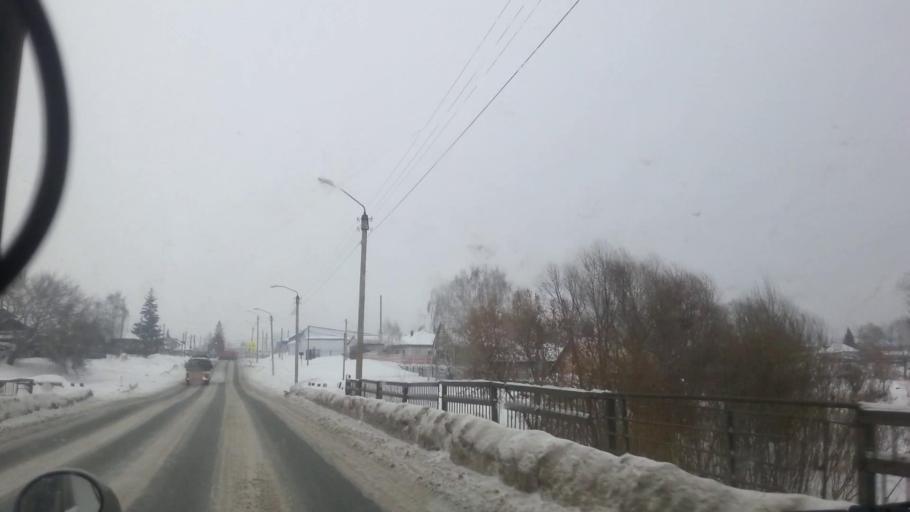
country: RU
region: Altai Krai
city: Vlasikha
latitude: 53.2953
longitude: 83.5798
